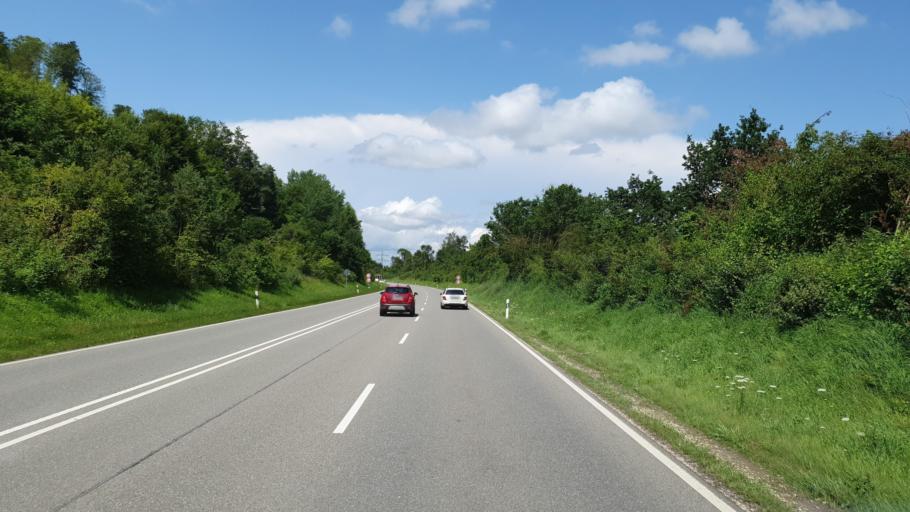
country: DE
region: Baden-Wuerttemberg
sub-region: Tuebingen Region
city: Sipplingen
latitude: 47.8099
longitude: 9.1177
